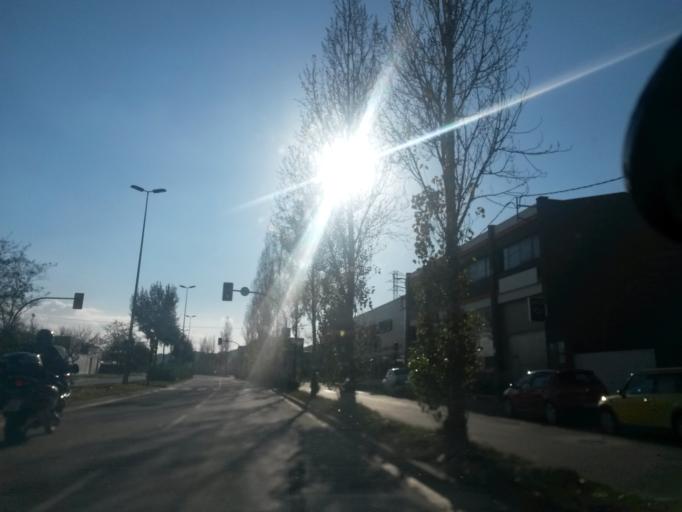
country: ES
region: Catalonia
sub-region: Provincia de Girona
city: Sarria de Ter
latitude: 42.0131
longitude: 2.8176
